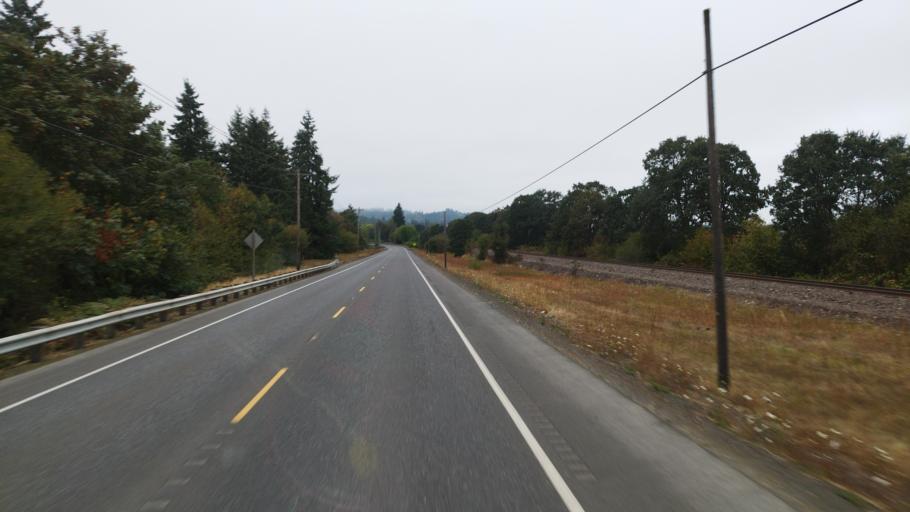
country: US
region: Oregon
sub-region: Columbia County
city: Columbia City
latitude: 45.9380
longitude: -122.8508
